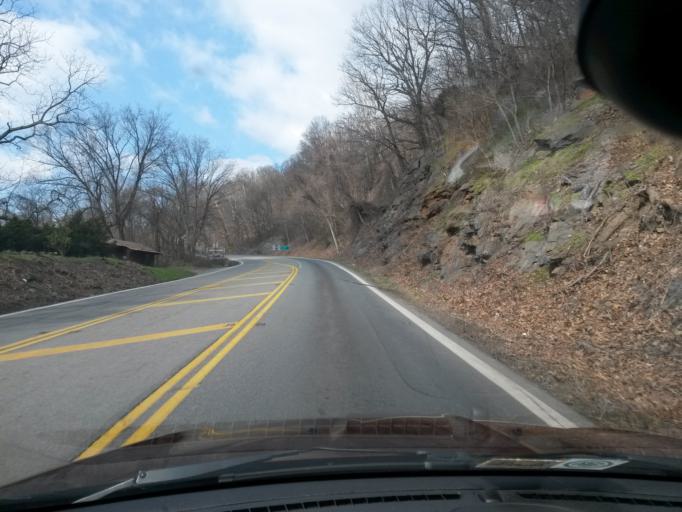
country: US
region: Virginia
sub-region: City of Waynesboro
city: Waynesboro
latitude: 38.0382
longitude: -78.8352
